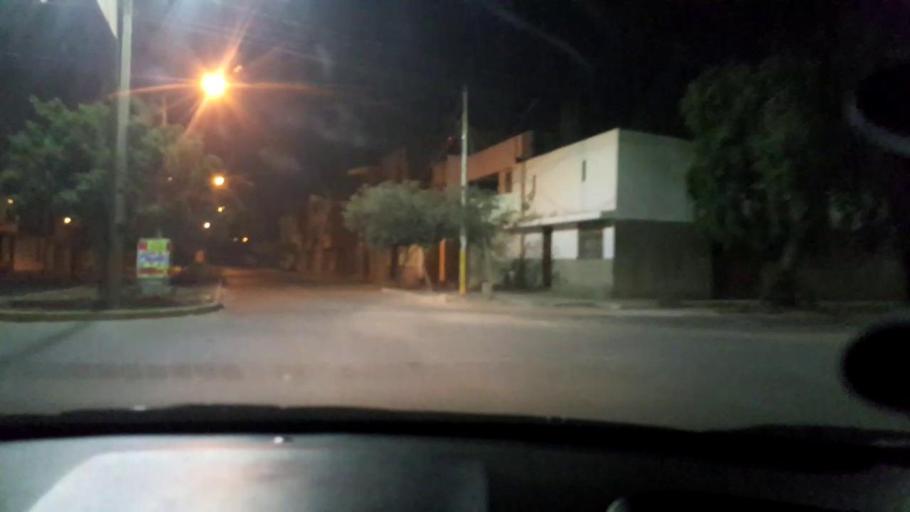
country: PE
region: Lambayeque
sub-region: Provincia de Chiclayo
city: Chiclayo
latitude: -6.7852
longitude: -79.8363
